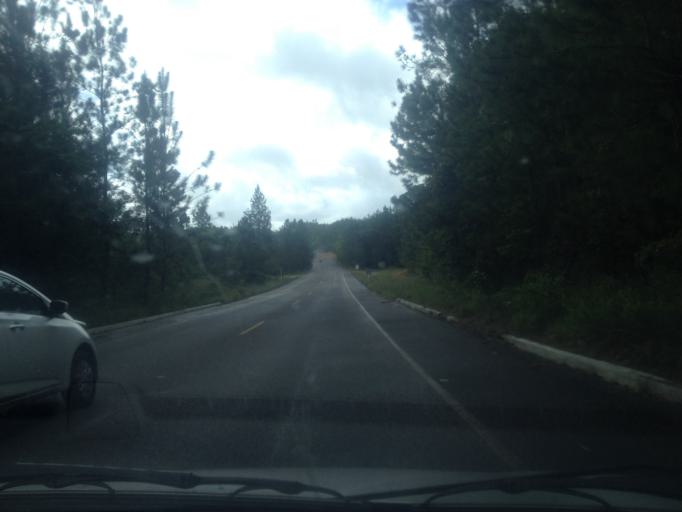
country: BR
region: Bahia
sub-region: Conde
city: Conde
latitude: -12.1003
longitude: -37.7787
